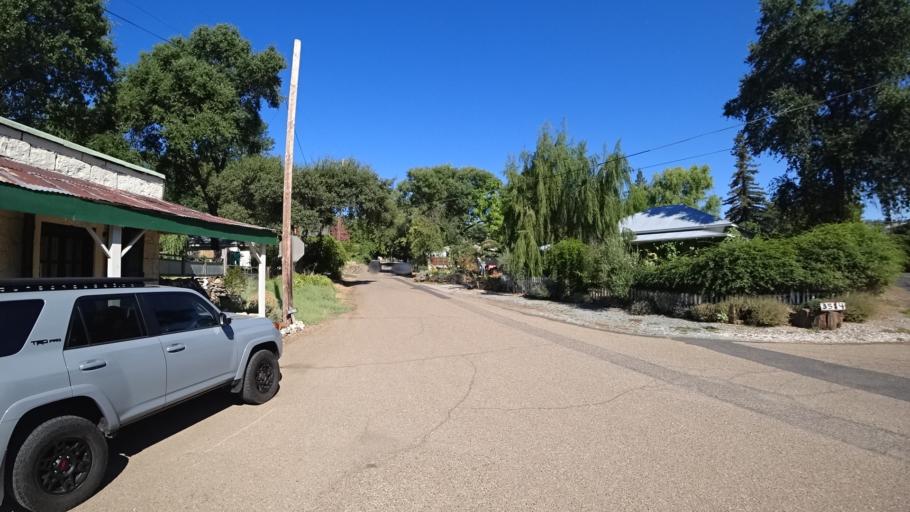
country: US
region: California
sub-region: Calaveras County
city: Murphys
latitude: 38.0855
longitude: -120.4729
